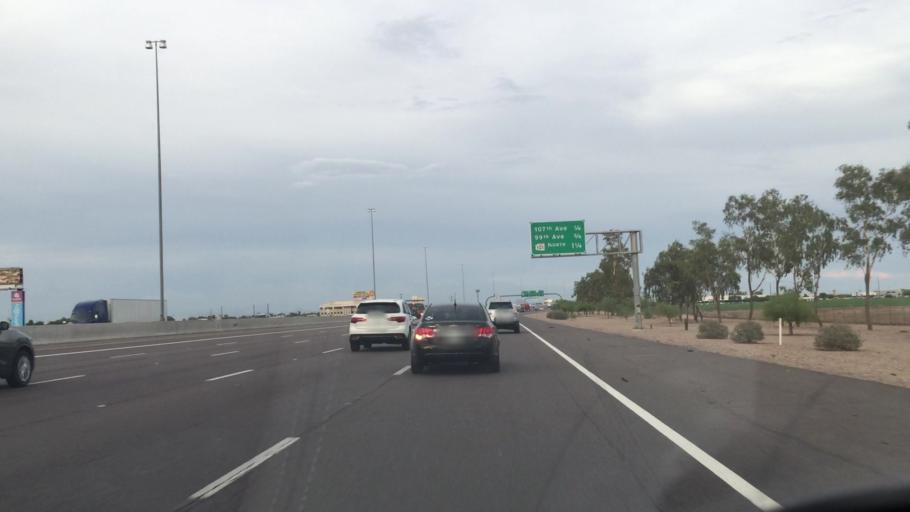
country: US
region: Arizona
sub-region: Maricopa County
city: Tolleson
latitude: 33.4602
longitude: -112.3006
